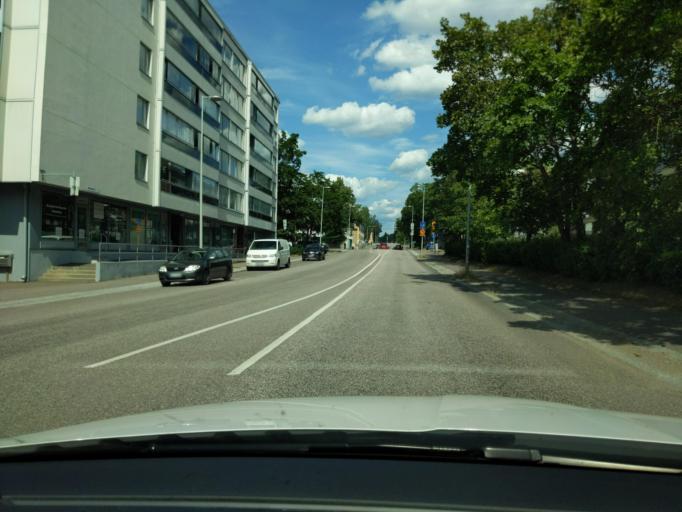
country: FI
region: Paijanne Tavastia
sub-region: Lahti
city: Heinola
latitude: 61.1998
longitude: 26.0345
